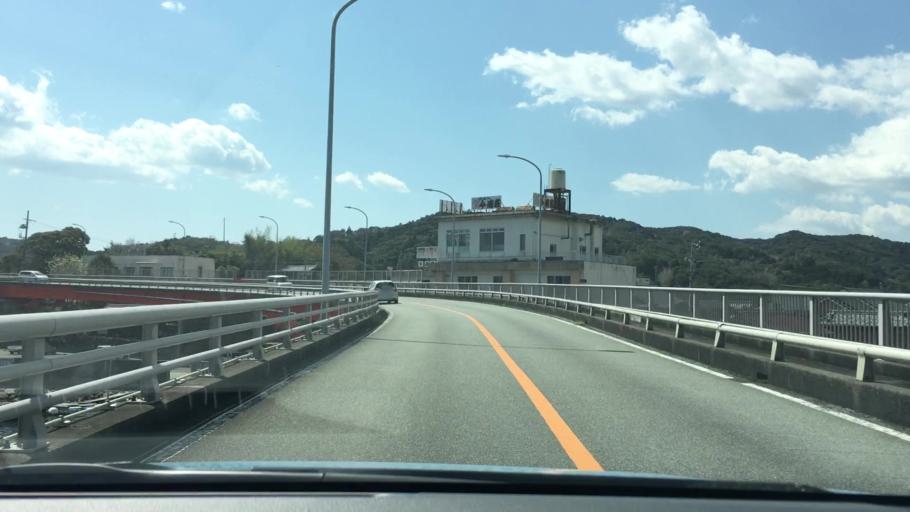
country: JP
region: Mie
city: Toba
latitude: 34.4421
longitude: 136.8804
